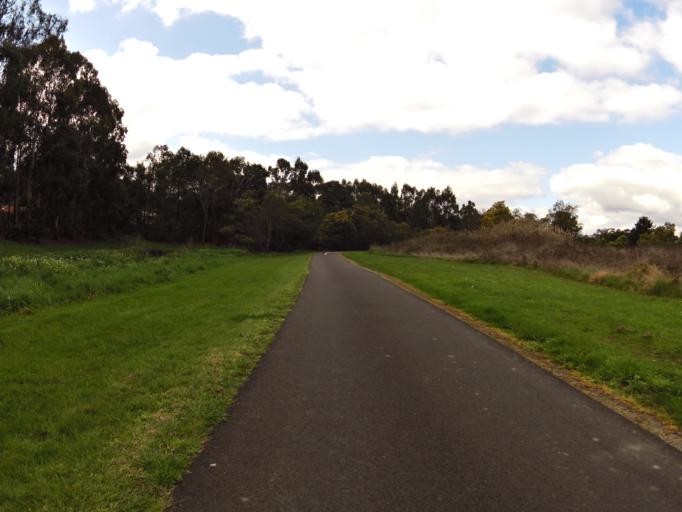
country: AU
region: Victoria
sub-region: Maroondah
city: Heathmont
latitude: -37.8383
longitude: 145.2455
